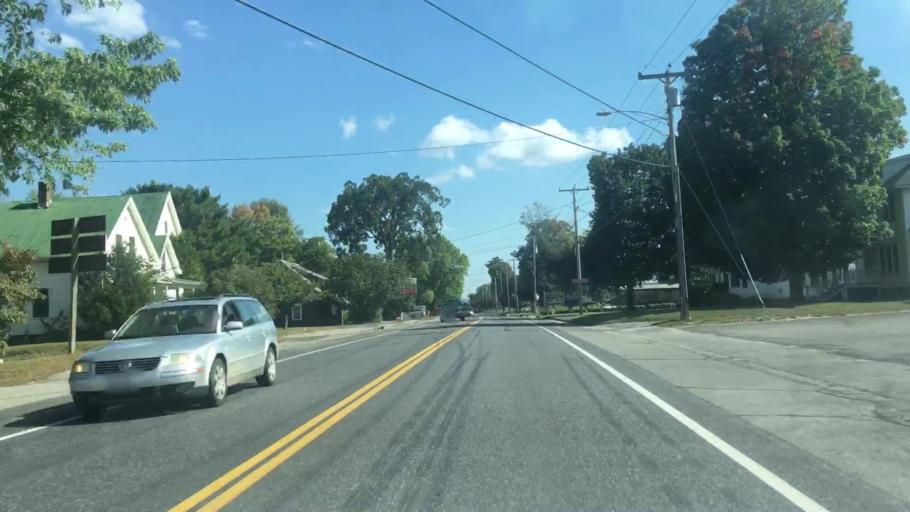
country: US
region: Maine
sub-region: Franklin County
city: Farmington
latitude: 44.6604
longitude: -70.1456
